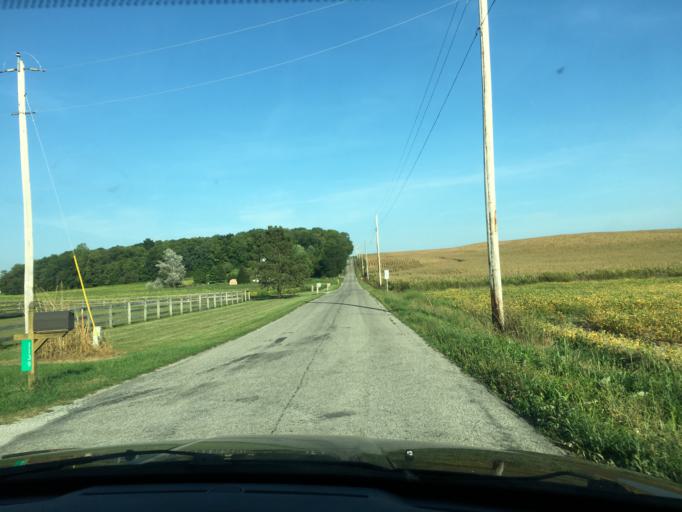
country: US
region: Ohio
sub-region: Logan County
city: West Liberty
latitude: 40.2991
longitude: -83.7408
